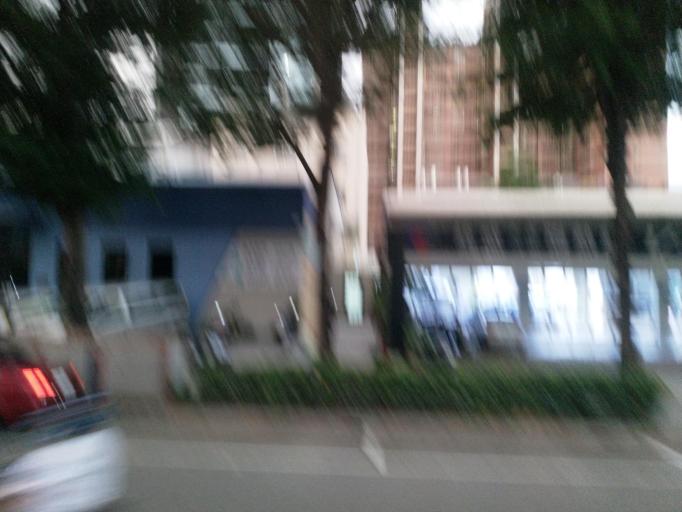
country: TW
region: Kaohsiung
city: Kaohsiung
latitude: 22.6835
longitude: 120.3127
